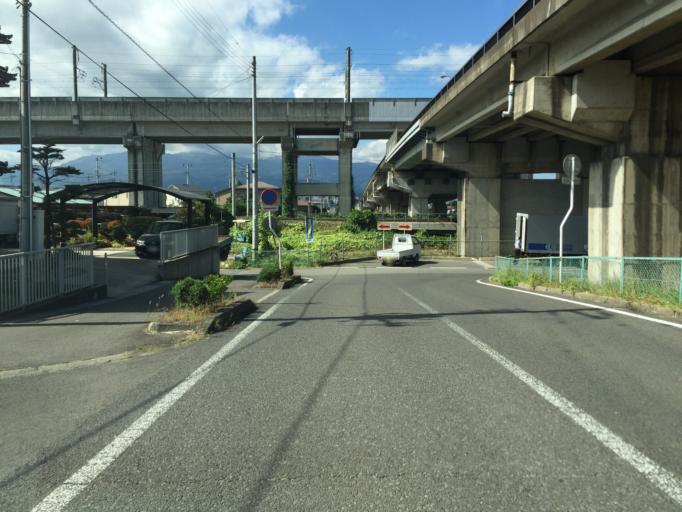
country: JP
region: Fukushima
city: Fukushima-shi
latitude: 37.7391
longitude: 140.4596
